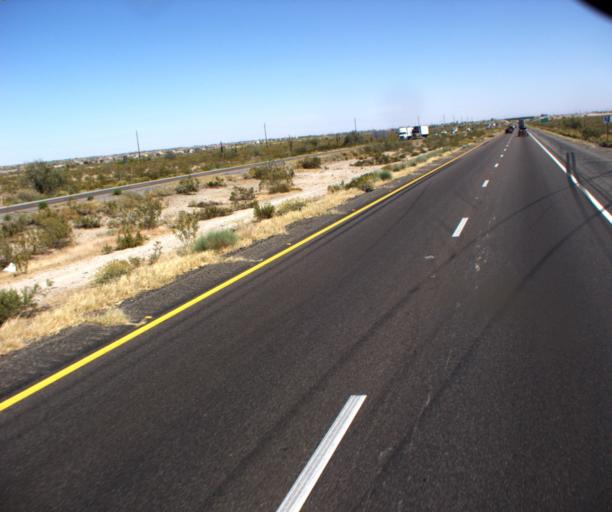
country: US
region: Arizona
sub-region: Maricopa County
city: Buckeye
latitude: 33.4548
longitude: -112.5247
